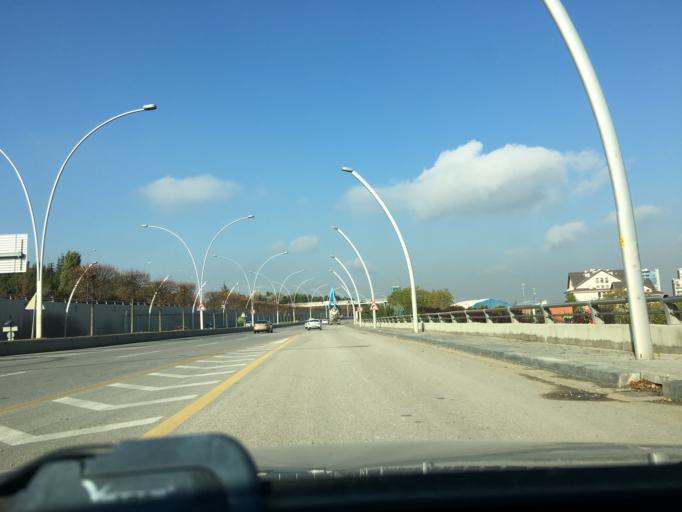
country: TR
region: Ankara
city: Ankara
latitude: 39.8901
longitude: 32.7971
